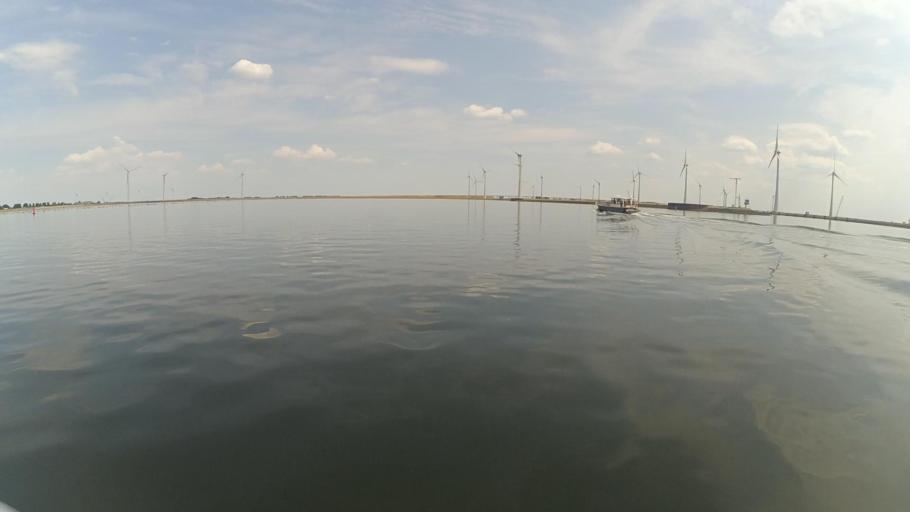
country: NL
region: Zeeland
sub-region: Schouwen-Duiveland
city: Bruinisse
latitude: 51.6638
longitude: 4.1338
